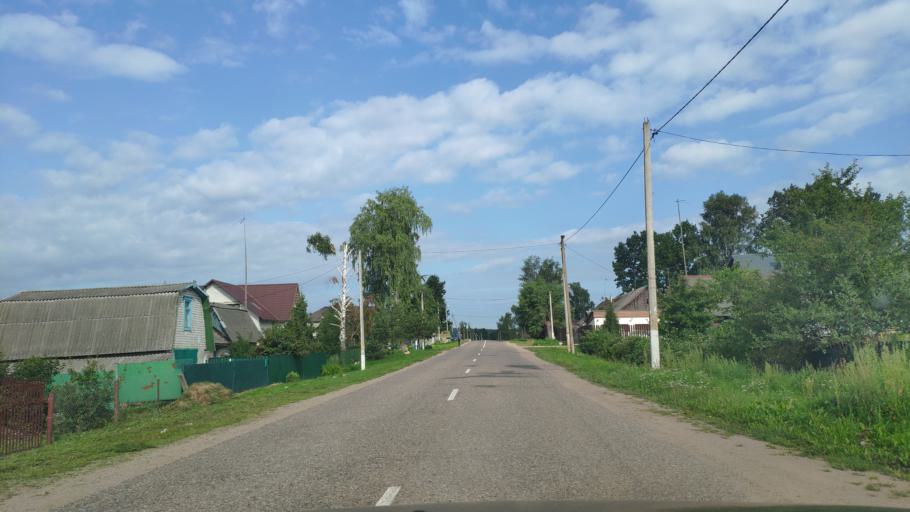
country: BY
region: Minsk
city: Khatsyezhyna
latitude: 53.8863
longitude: 27.2681
